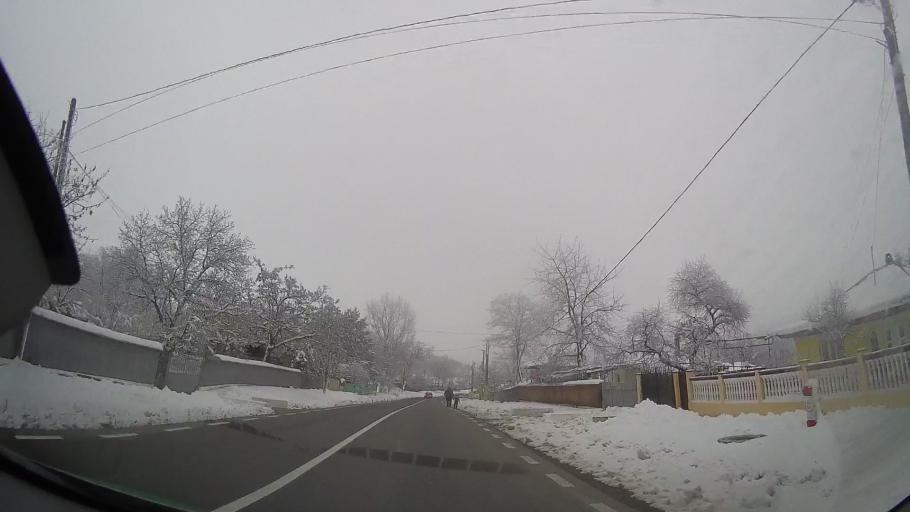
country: RO
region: Neamt
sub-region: Comuna Poenari
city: Poienari
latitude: 46.8864
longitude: 27.1308
